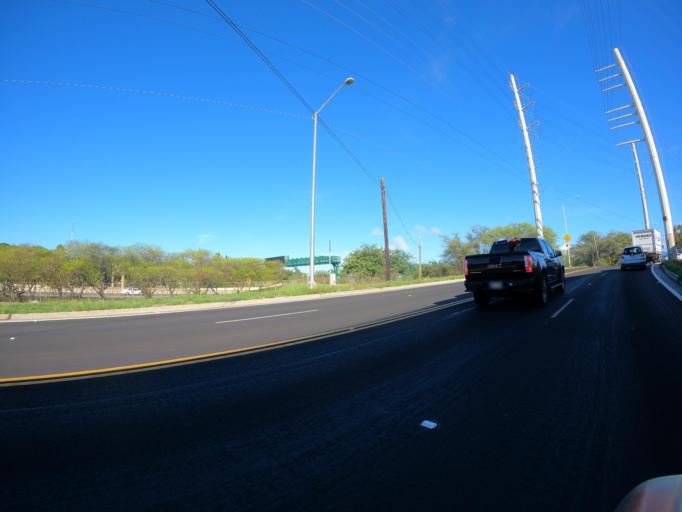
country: US
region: Hawaii
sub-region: Honolulu County
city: Halawa
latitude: 21.3546
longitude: -157.9314
